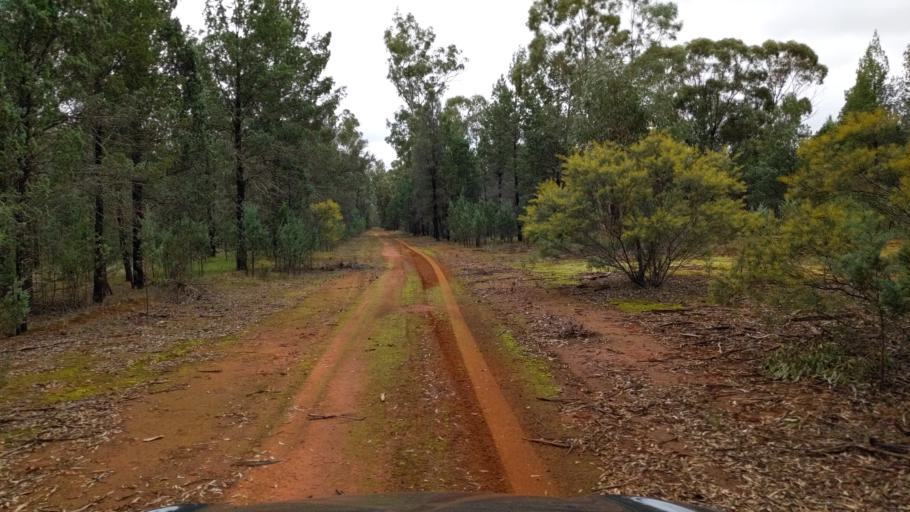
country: AU
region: New South Wales
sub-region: Coolamon
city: Coolamon
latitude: -34.8409
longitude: 146.9337
